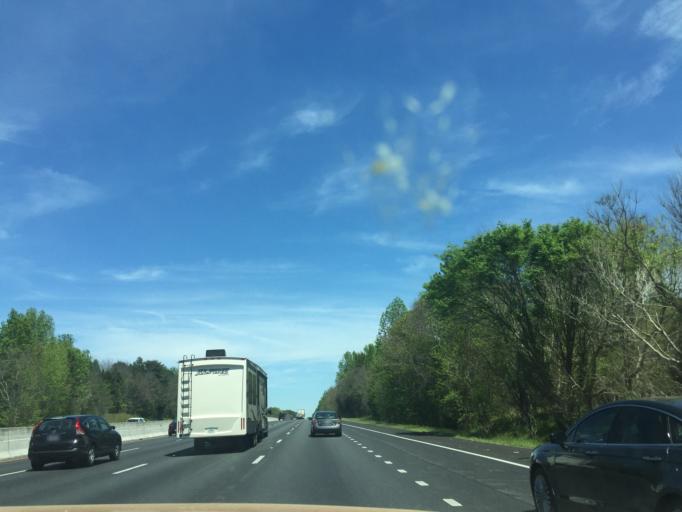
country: US
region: South Carolina
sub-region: York County
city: Fort Mill
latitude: 35.0655
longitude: -80.9529
